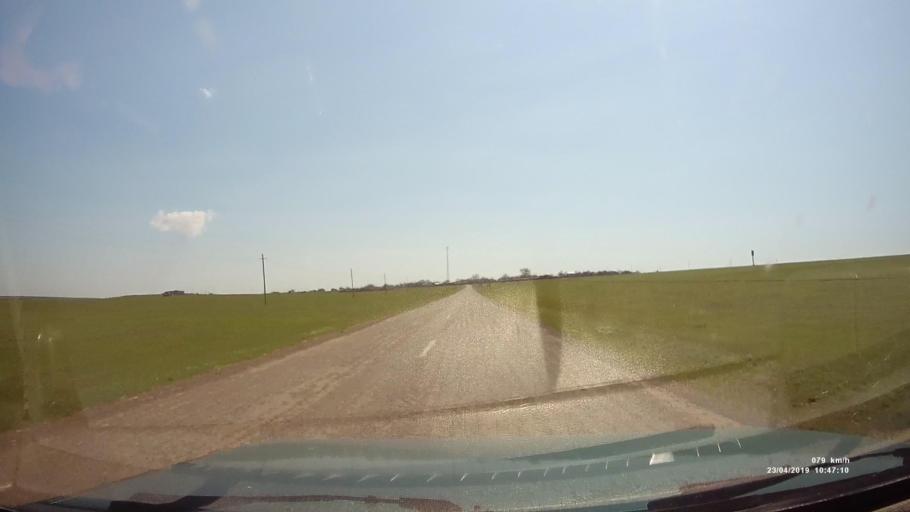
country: RU
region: Kalmykiya
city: Yashalta
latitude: 46.4373
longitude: 42.7026
